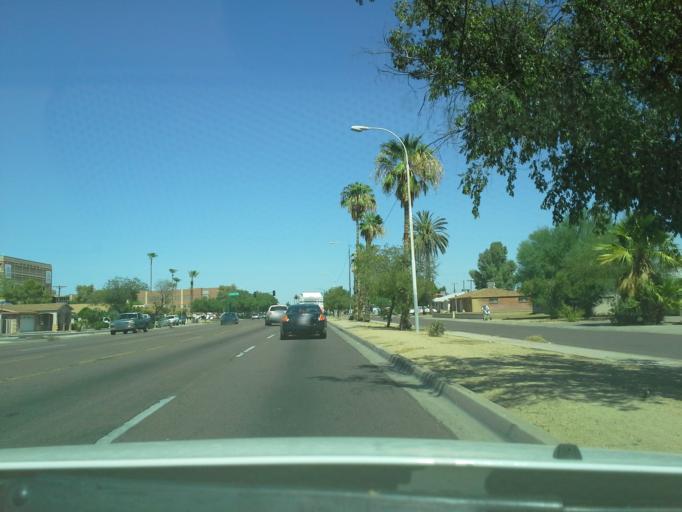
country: US
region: Arizona
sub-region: Maricopa County
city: Glendale
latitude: 33.5240
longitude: -112.1060
